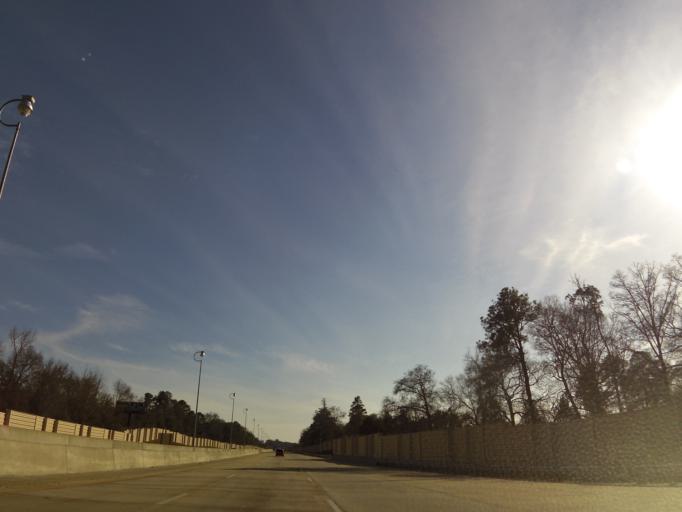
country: US
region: Georgia
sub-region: Muscogee County
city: Columbus
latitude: 32.4419
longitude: -84.9275
